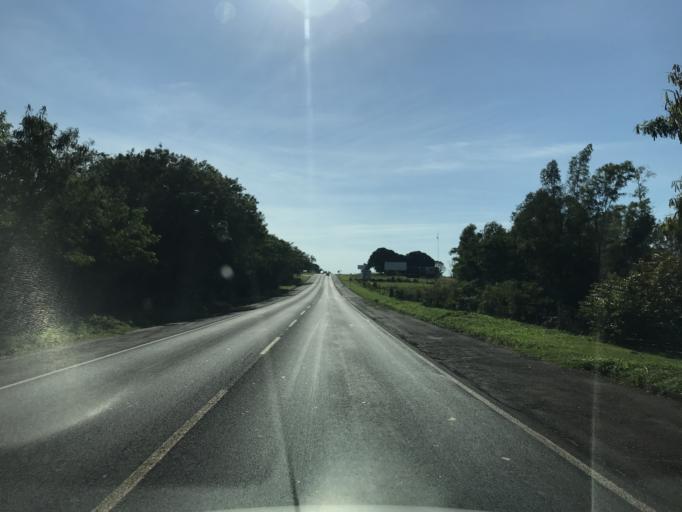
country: BR
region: Parana
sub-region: Umuarama
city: Umuarama
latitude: -23.8366
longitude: -53.3586
